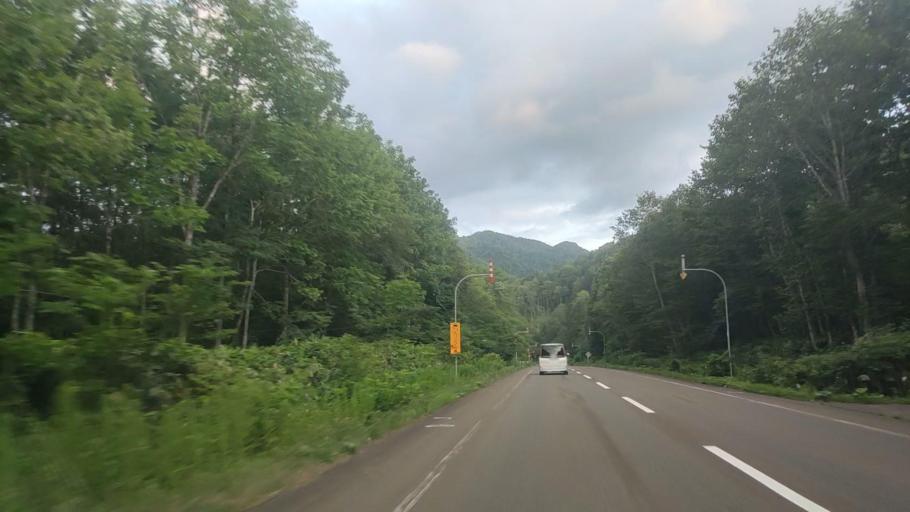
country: JP
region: Hokkaido
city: Ashibetsu
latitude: 43.3719
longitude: 142.2241
